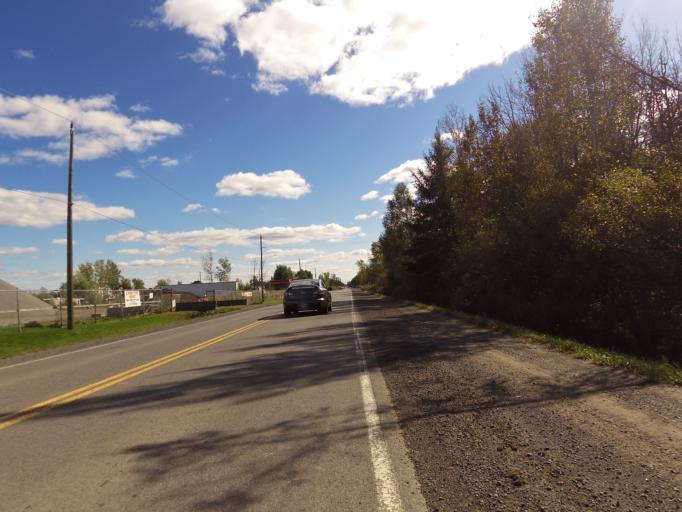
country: CA
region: Ontario
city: Clarence-Rockland
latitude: 45.3413
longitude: -75.4413
